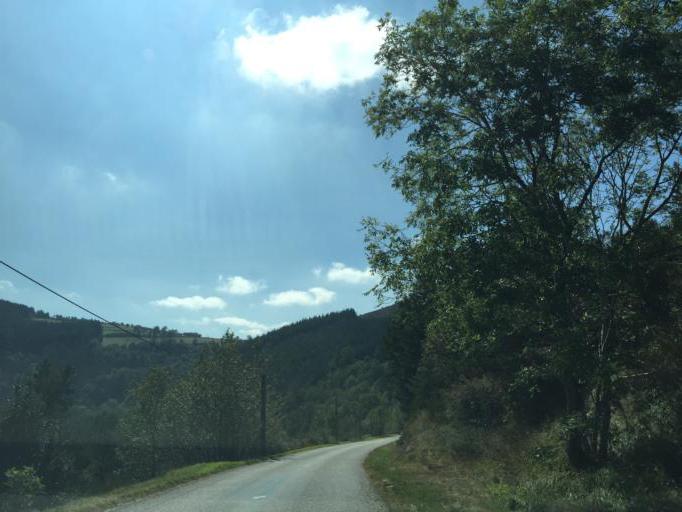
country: FR
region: Rhone-Alpes
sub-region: Departement de la Loire
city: Saint-Chamond
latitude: 45.4232
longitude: 4.5529
